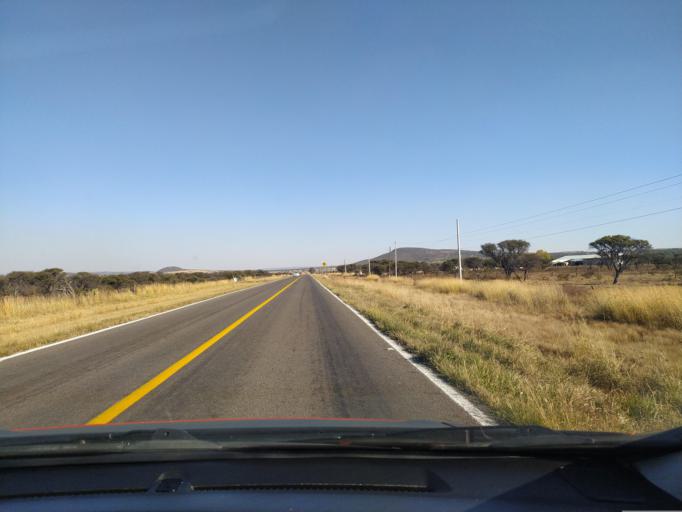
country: MX
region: Jalisco
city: San Miguel el Alto
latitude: 21.0172
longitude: -102.4941
